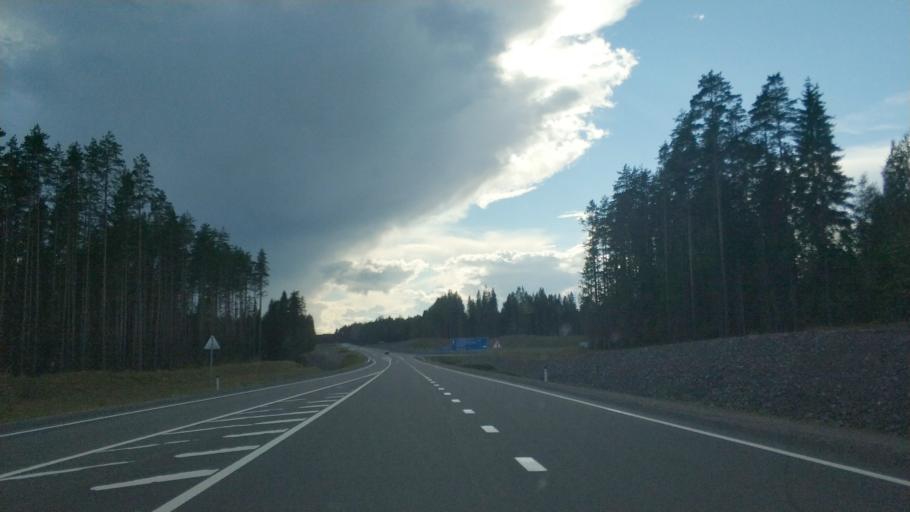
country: RU
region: Republic of Karelia
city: Lakhdenpokh'ya
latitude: 61.5025
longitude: 30.0381
